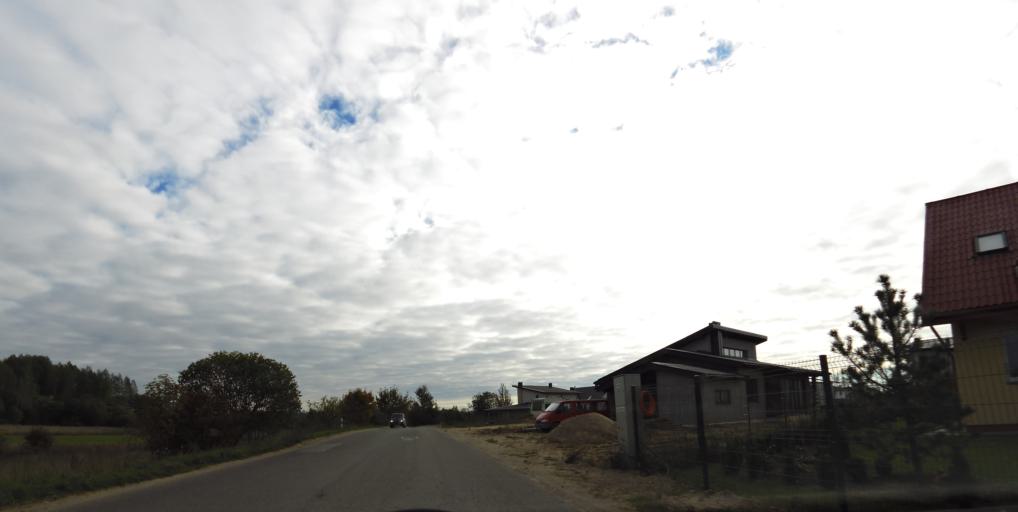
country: LT
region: Vilnius County
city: Pilaite
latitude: 54.7218
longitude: 25.1555
